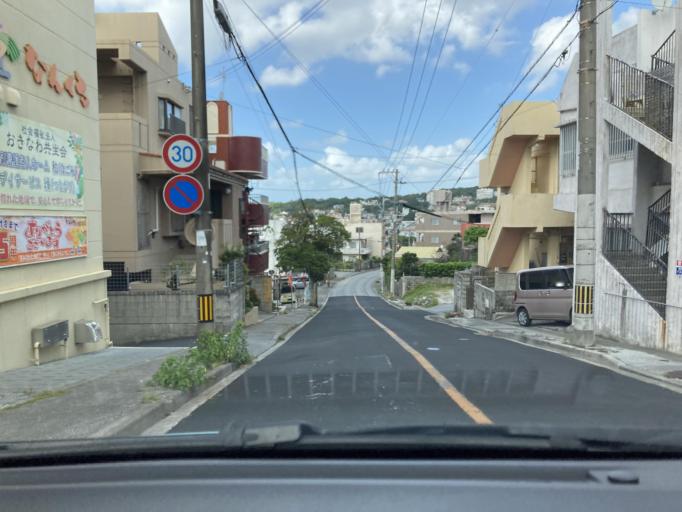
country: JP
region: Okinawa
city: Naha-shi
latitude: 26.2089
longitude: 127.7115
